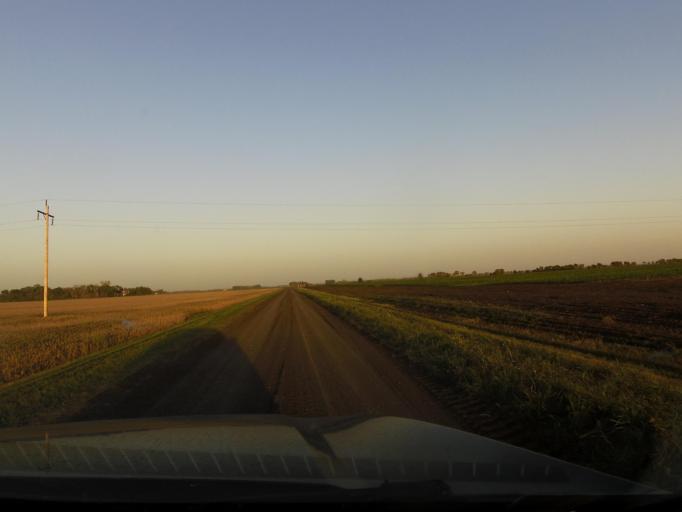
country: US
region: North Dakota
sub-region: Walsh County
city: Grafton
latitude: 48.3831
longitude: -97.2328
